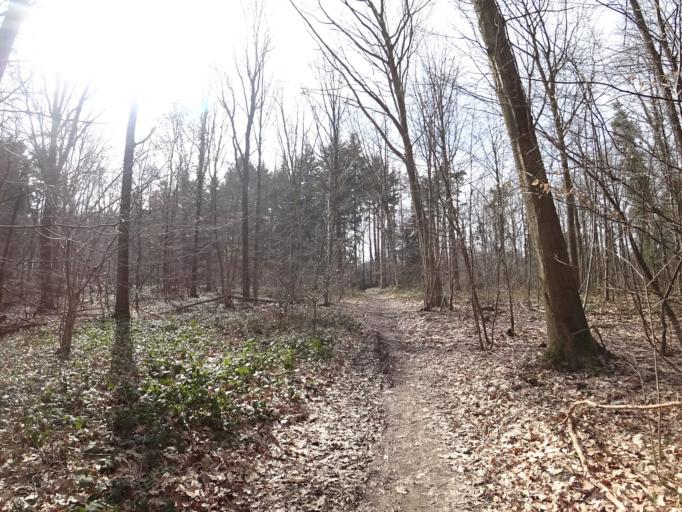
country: BE
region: Wallonia
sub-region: Province de Namur
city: Namur
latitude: 50.4339
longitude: 4.8273
